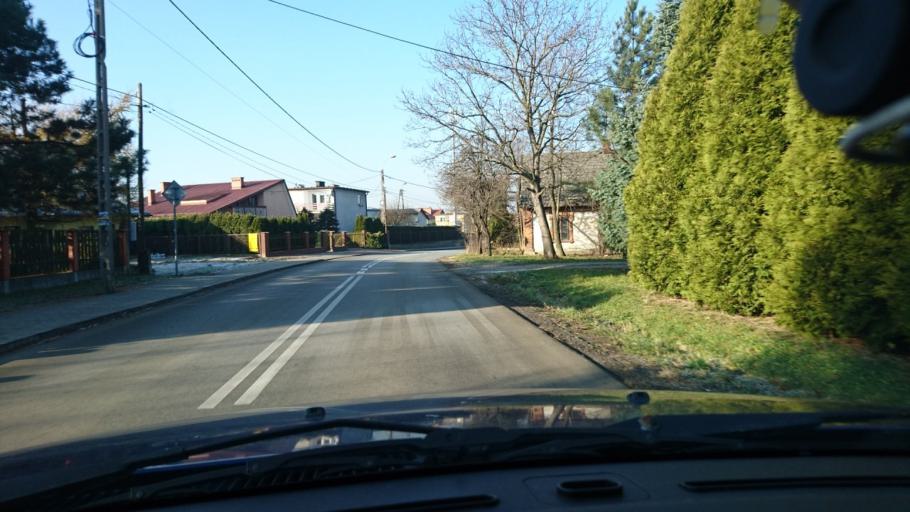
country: PL
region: Silesian Voivodeship
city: Janowice
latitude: 49.8839
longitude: 19.0975
